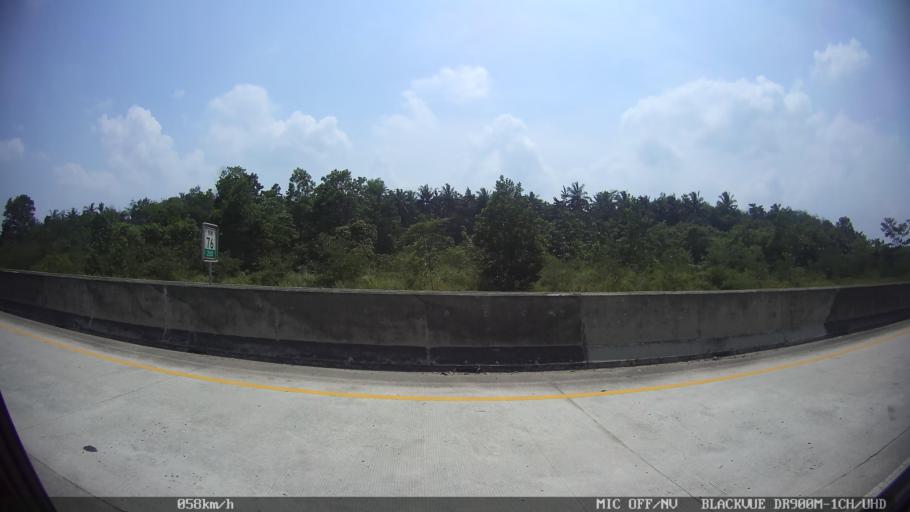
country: ID
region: Lampung
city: Kedaton
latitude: -5.3852
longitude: 105.3372
